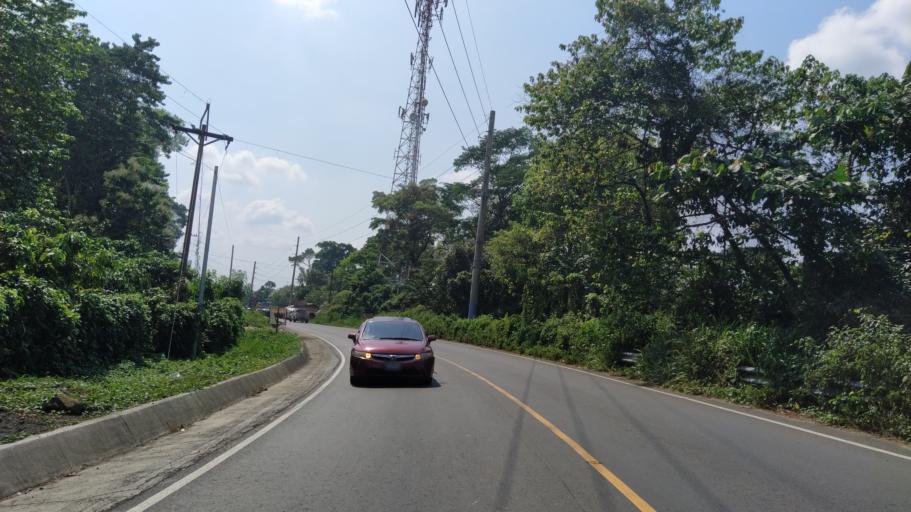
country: GT
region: Retalhuleu
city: San Felipe
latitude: 14.6228
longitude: -91.5859
